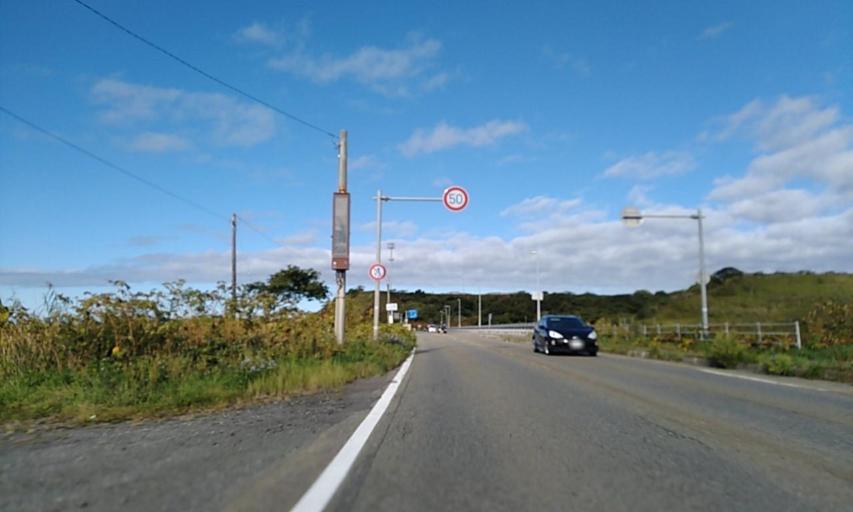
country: JP
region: Hokkaido
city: Shizunai-furukawacho
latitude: 42.2465
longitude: 142.5755
